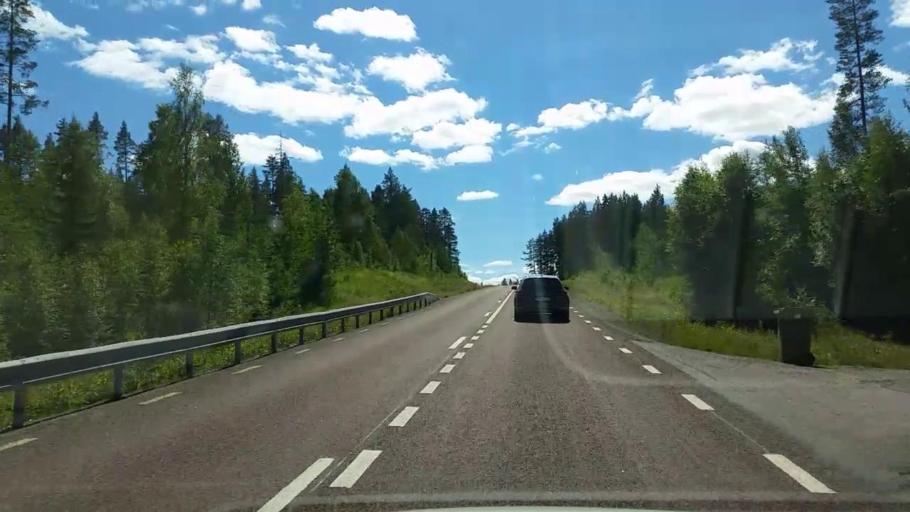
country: SE
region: Gaevleborg
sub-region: Ovanakers Kommun
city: Edsbyn
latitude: 61.2138
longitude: 15.8738
